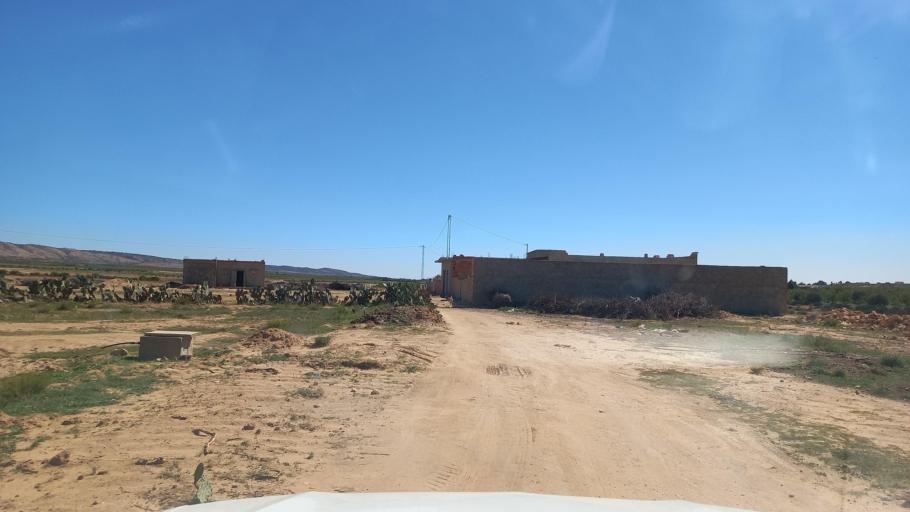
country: TN
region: Al Qasrayn
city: Sbiba
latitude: 35.3594
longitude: 9.0863
